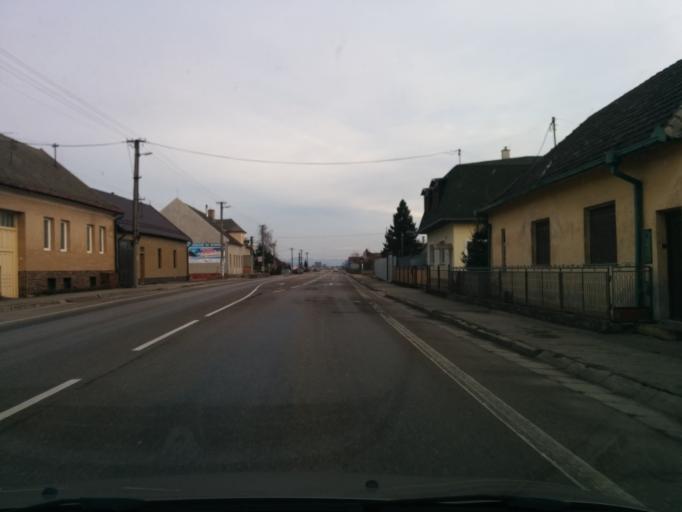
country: SK
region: Trnavsky
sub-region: Okres Trnava
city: Piestany
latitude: 48.6577
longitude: 17.8412
